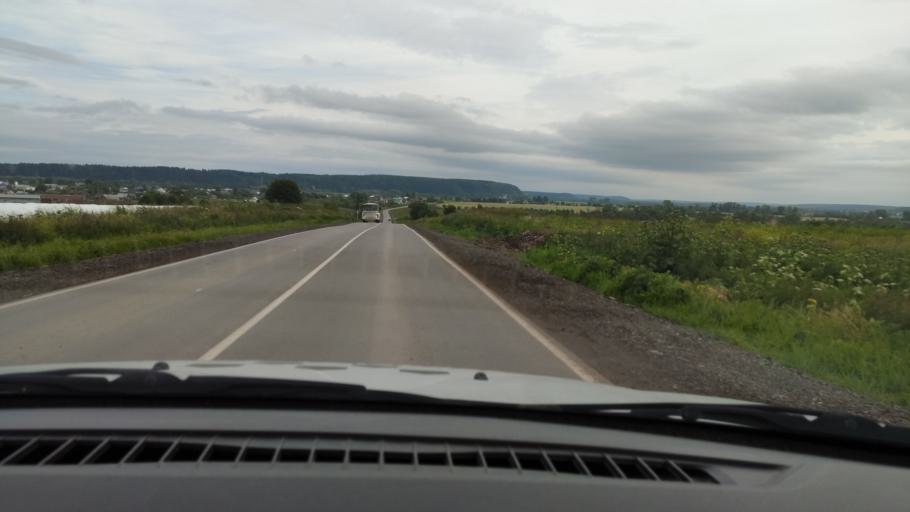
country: RU
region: Perm
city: Orda
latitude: 57.3093
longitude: 56.6459
